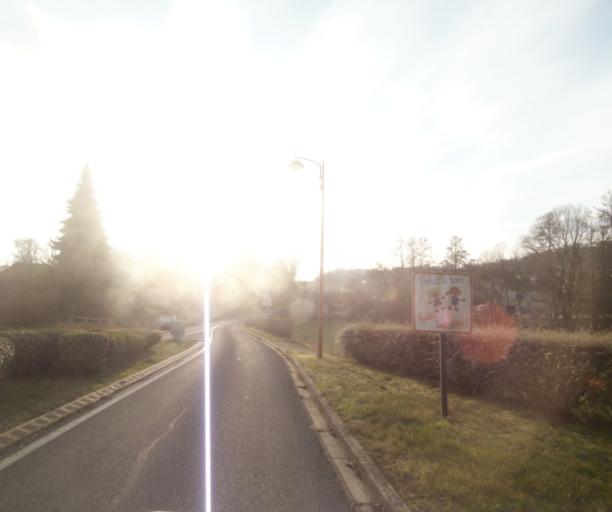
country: FR
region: Champagne-Ardenne
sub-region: Departement de la Marne
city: Sermaize-les-Bains
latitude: 48.7233
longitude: 4.9408
